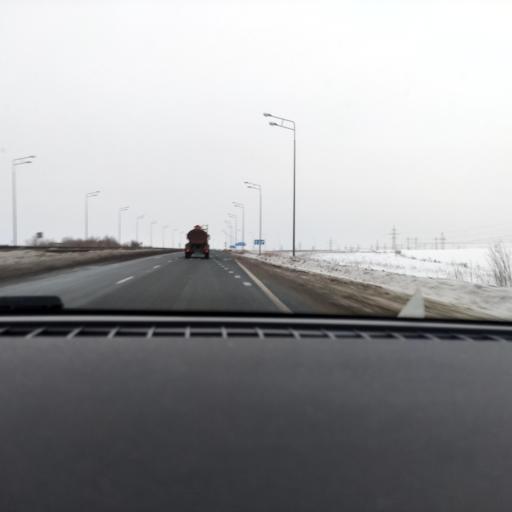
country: RU
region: Samara
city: Smyshlyayevka
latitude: 53.1301
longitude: 50.4228
